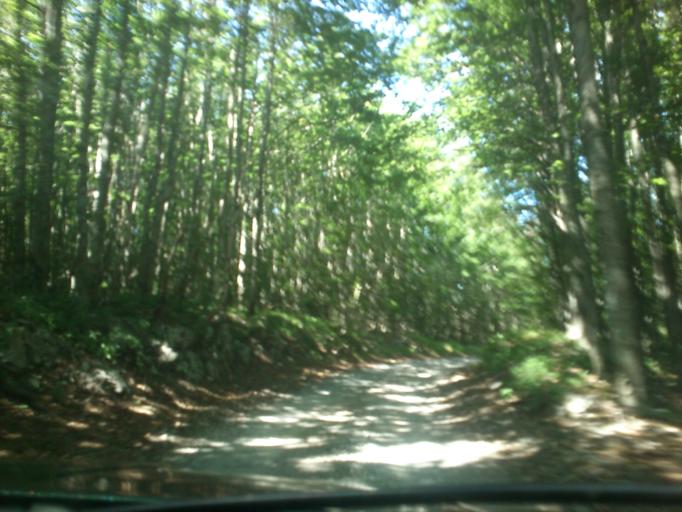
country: HR
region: Licko-Senjska
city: Senj
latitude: 44.8274
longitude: 14.9794
